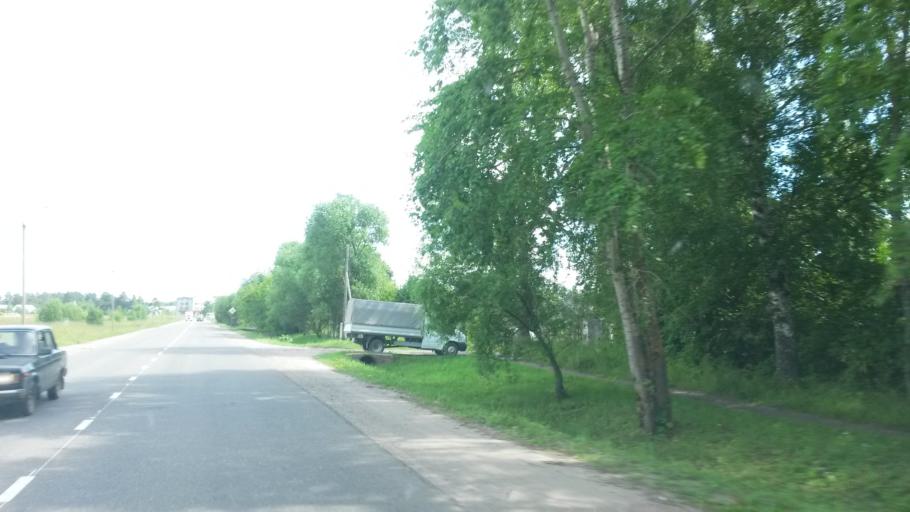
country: RU
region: Ivanovo
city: Zavolzhsk
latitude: 57.4985
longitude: 42.1258
